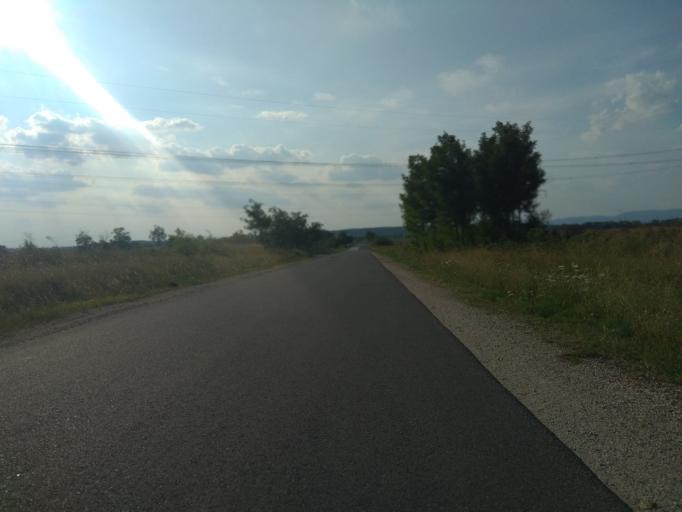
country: HU
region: Borsod-Abauj-Zemplen
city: Emod
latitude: 47.8928
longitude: 20.7591
